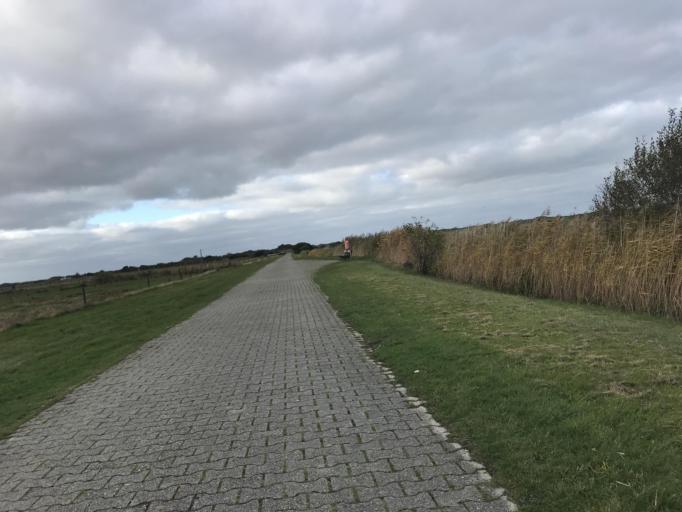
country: DE
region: Lower Saxony
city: Borkum
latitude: 53.5952
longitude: 6.7403
